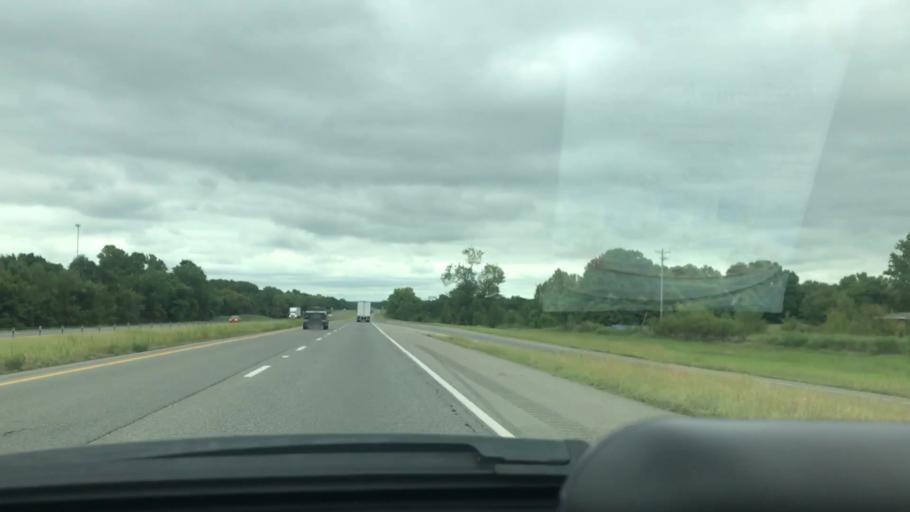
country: US
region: Oklahoma
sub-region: McIntosh County
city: Eufaula
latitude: 35.3640
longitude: -95.5733
